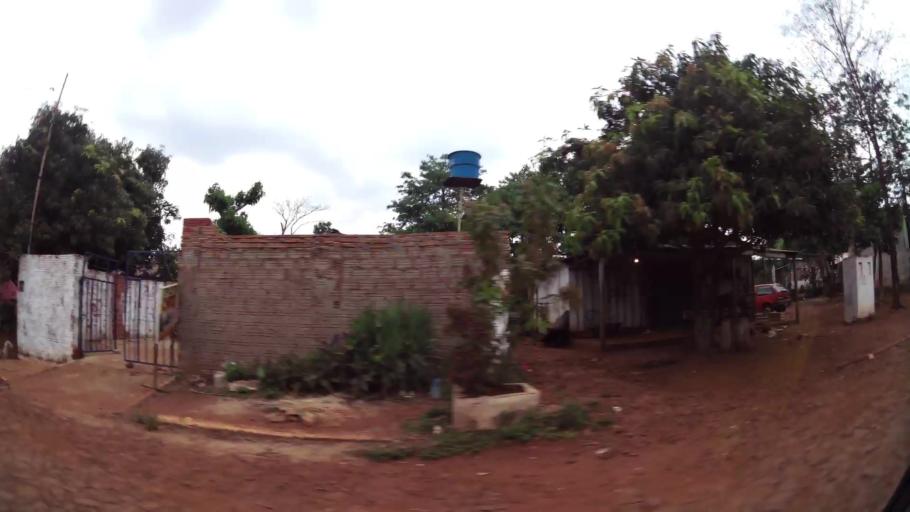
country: PY
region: Alto Parana
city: Presidente Franco
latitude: -25.5478
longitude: -54.6541
